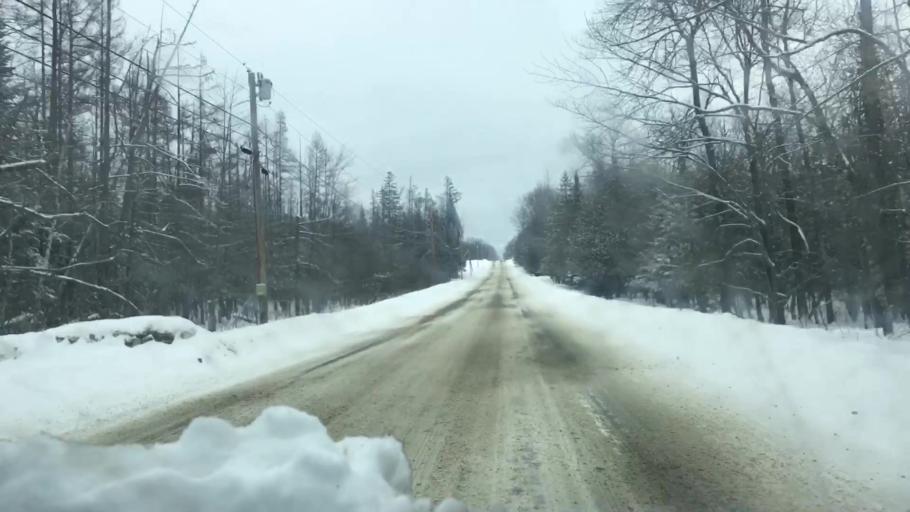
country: US
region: Maine
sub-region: Penobscot County
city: Bradford
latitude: 45.0118
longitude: -68.9927
